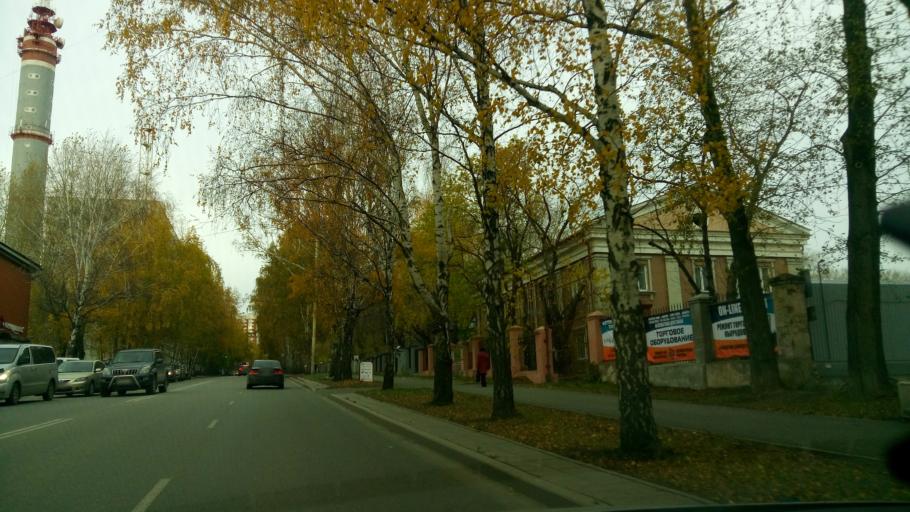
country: RU
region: Sverdlovsk
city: Yekaterinburg
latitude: 56.8453
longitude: 60.6334
